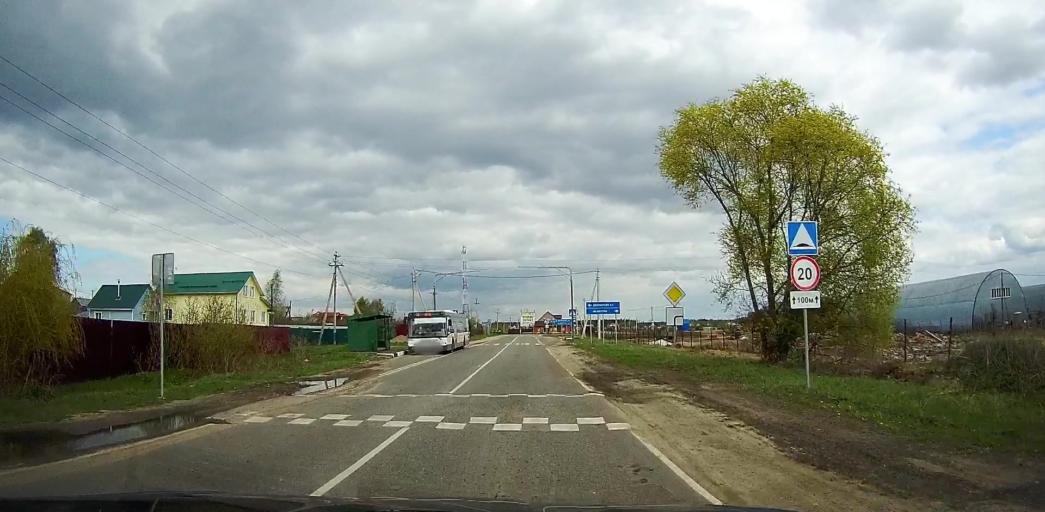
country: RU
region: Moskovskaya
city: Imeni Tsyurupy
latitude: 55.4963
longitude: 38.6221
